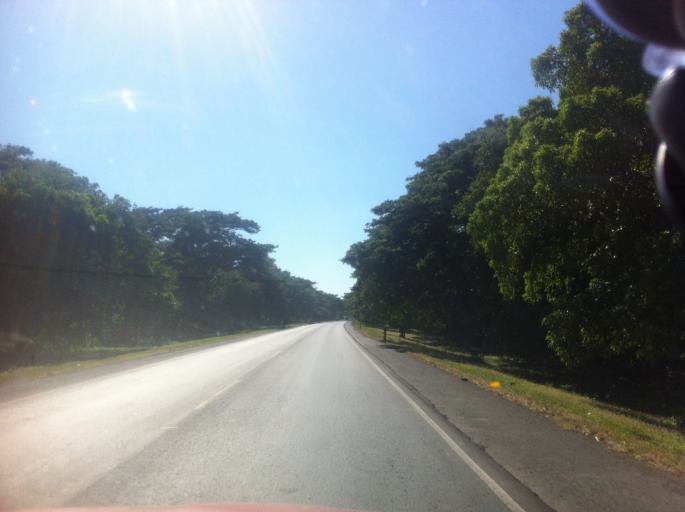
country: NI
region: Managua
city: Tipitapa
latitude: 12.1626
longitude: -86.1290
